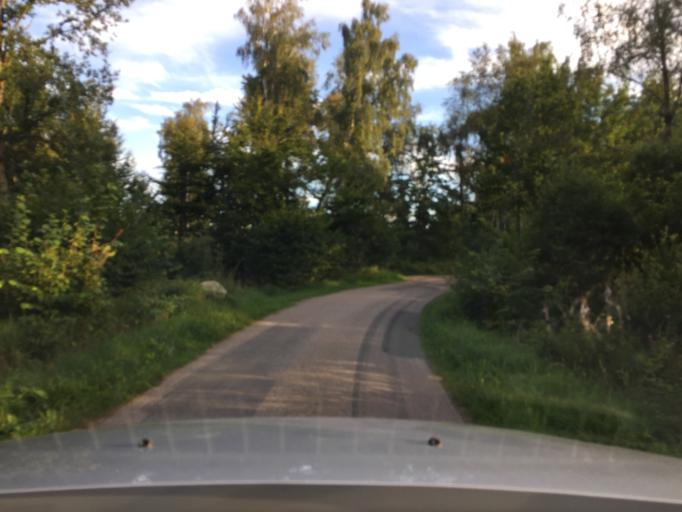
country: SE
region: Skane
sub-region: Hassleholms Kommun
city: Sosdala
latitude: 55.9941
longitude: 13.6063
